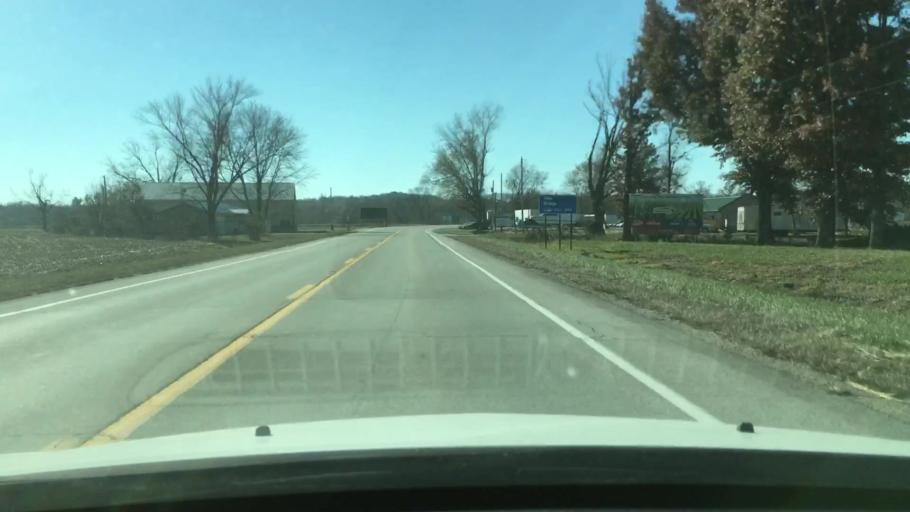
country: US
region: Missouri
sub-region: Pike County
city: Louisiana
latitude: 39.4640
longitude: -91.0296
